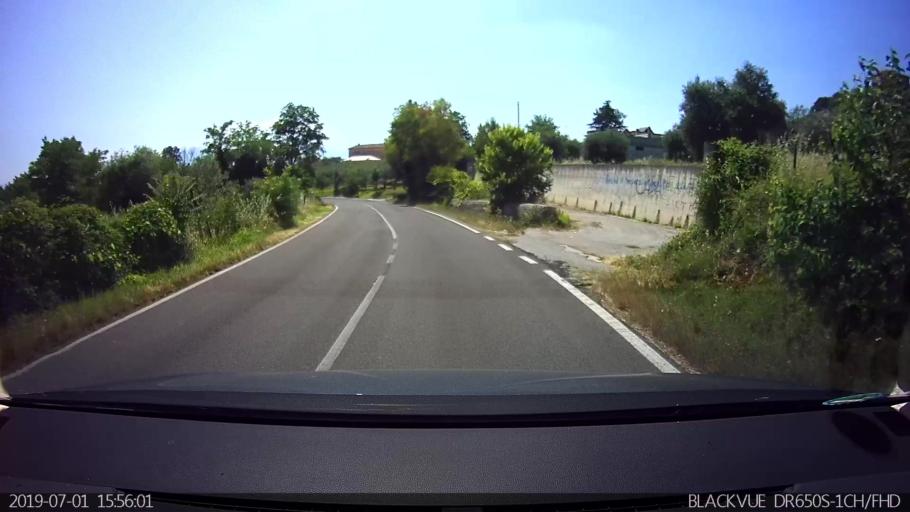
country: IT
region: Latium
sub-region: Provincia di Frosinone
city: Veroli
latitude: 41.6850
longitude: 13.4207
